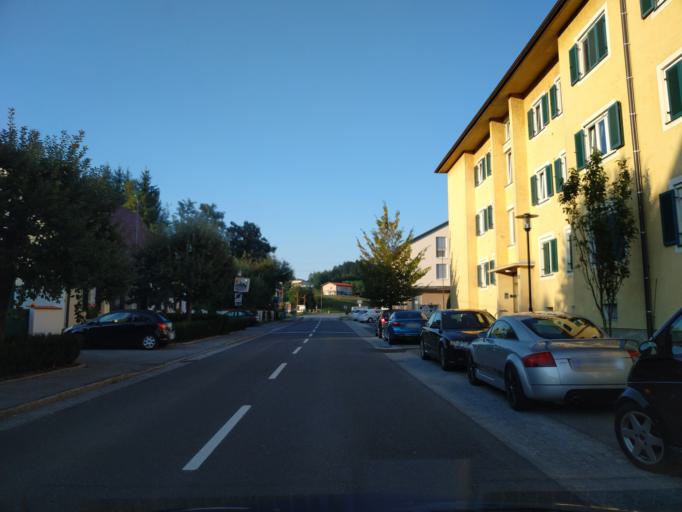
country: AT
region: Styria
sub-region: Politischer Bezirk Deutschlandsberg
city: Wies
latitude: 46.7206
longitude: 15.2727
